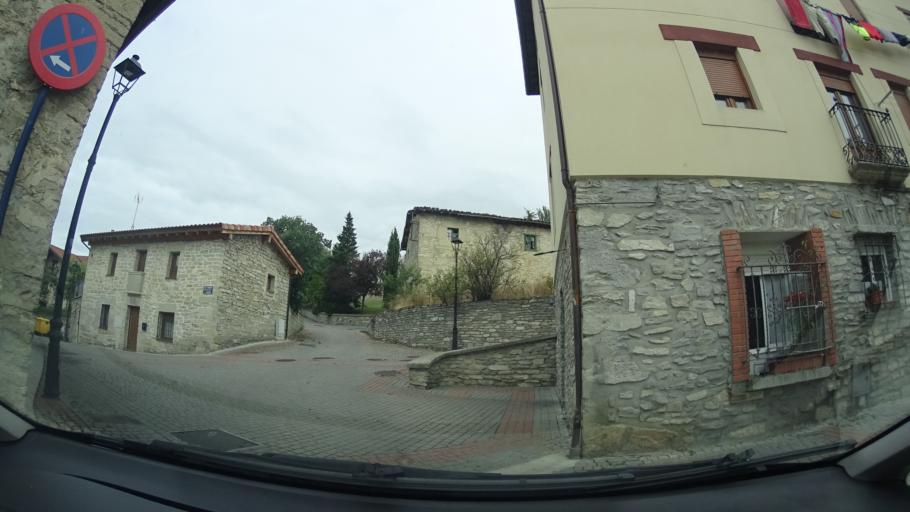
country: ES
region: Basque Country
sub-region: Provincia de Alava
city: Arminon
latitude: 42.8177
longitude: -2.8105
